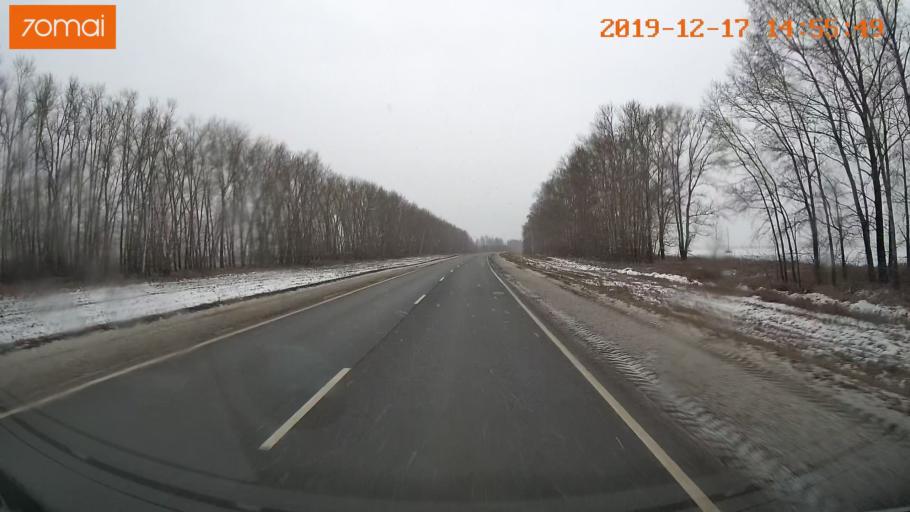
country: RU
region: Rjazan
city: Zakharovo
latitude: 54.3477
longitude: 39.2604
